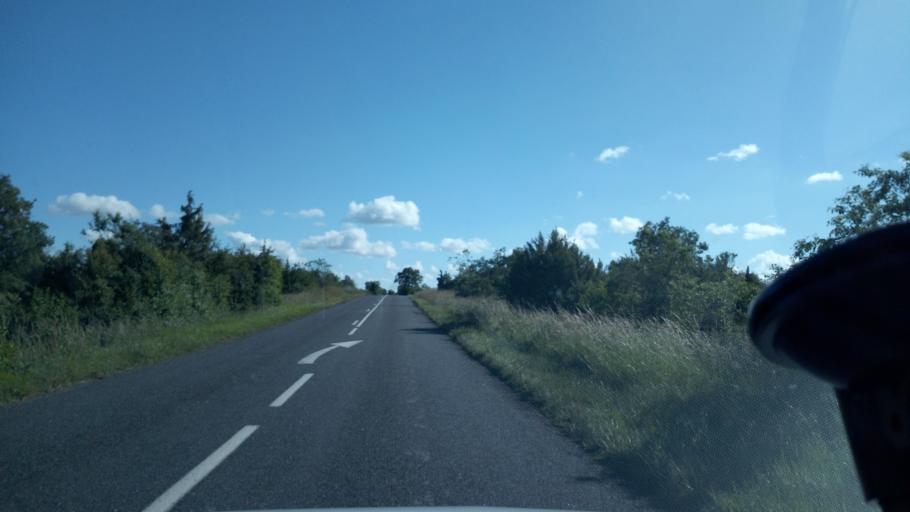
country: FR
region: Midi-Pyrenees
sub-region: Departement de l'Aveyron
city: Sebazac-Concoures
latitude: 44.4279
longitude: 2.6149
